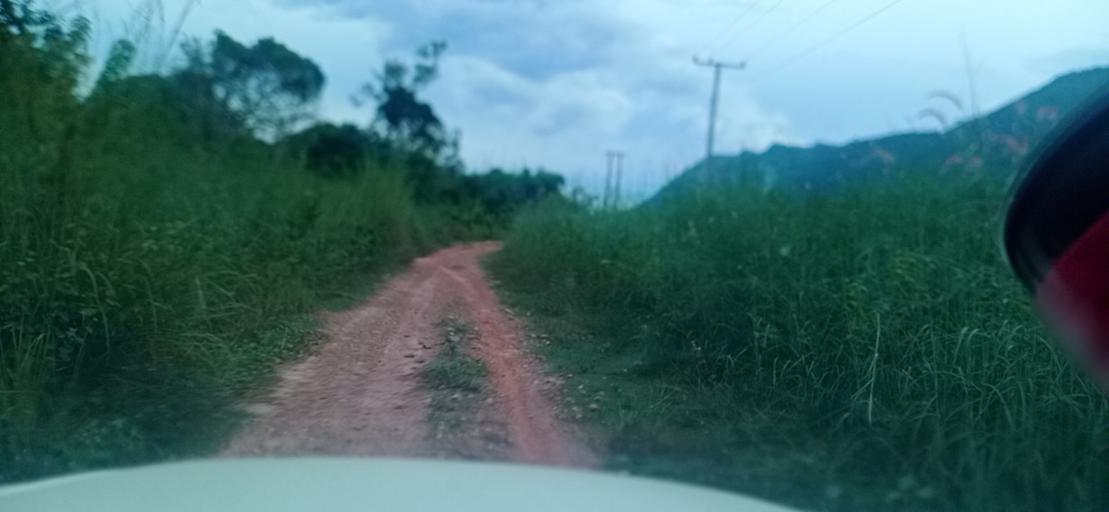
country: TH
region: Changwat Bueng Kan
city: Pak Khat
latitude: 18.5624
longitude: 103.2870
